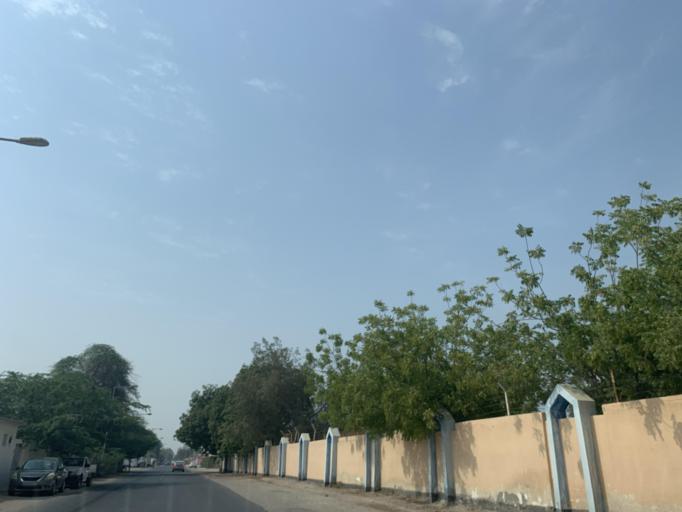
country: BH
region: Manama
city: Jidd Hafs
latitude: 26.2143
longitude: 50.4879
